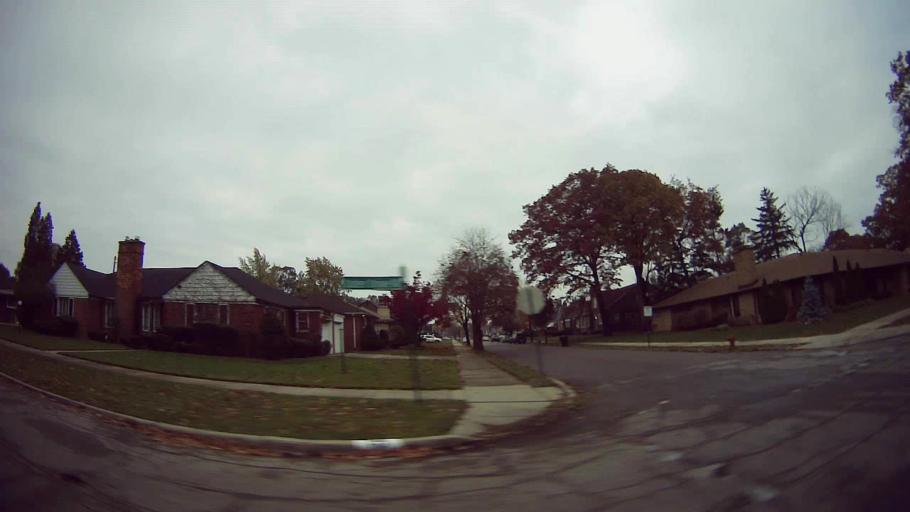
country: US
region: Michigan
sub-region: Oakland County
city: Ferndale
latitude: 42.4352
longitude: -83.1448
